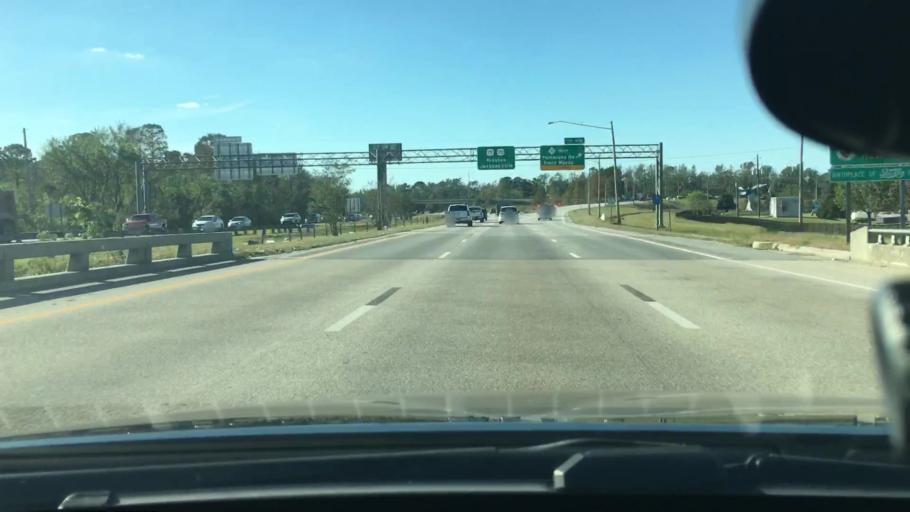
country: US
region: North Carolina
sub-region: Craven County
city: New Bern
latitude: 35.0996
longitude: -77.0536
